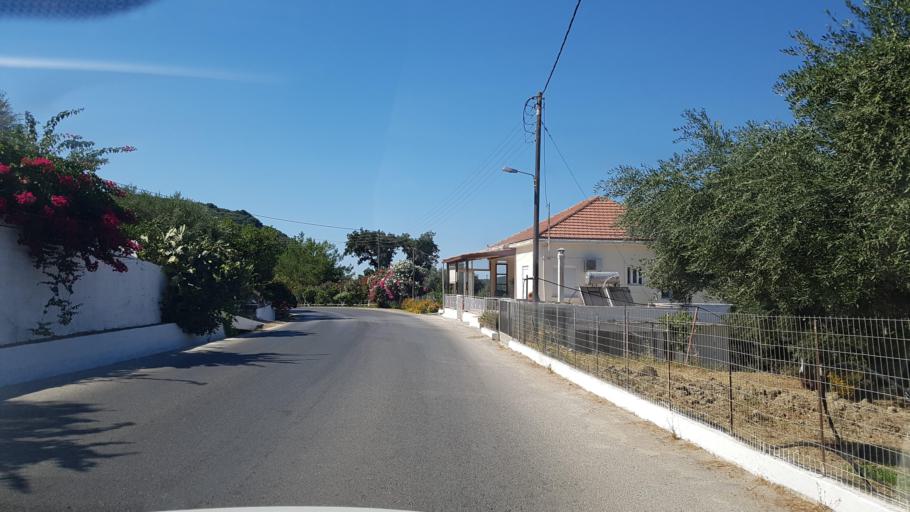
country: GR
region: Crete
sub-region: Nomos Chanias
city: Kissamos
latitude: 35.4655
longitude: 23.6962
